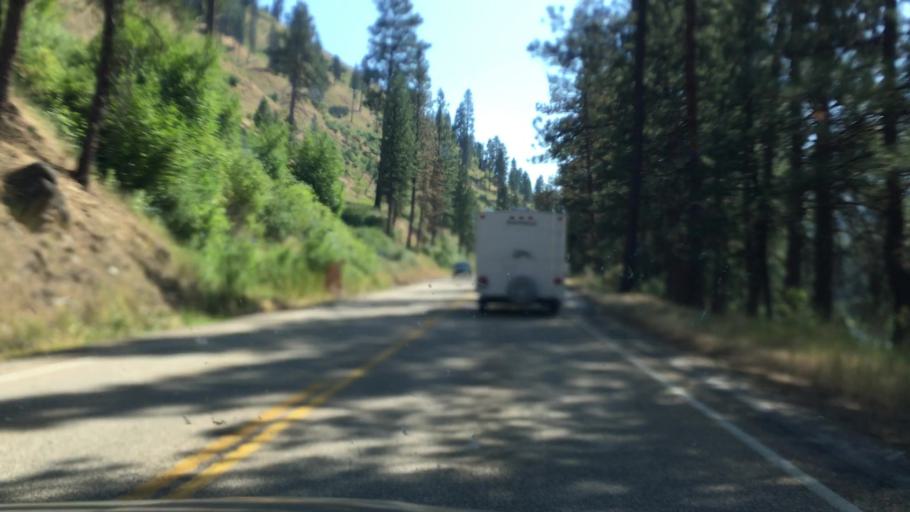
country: US
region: Idaho
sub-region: Boise County
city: Idaho City
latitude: 44.0632
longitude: -116.1219
